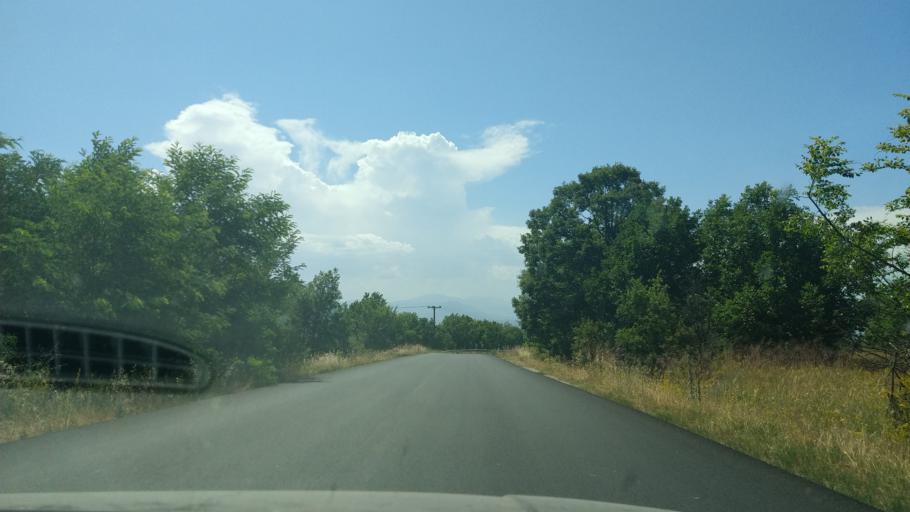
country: GR
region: West Macedonia
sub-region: Nomos Grevenon
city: Grevena
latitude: 39.9729
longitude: 21.5206
